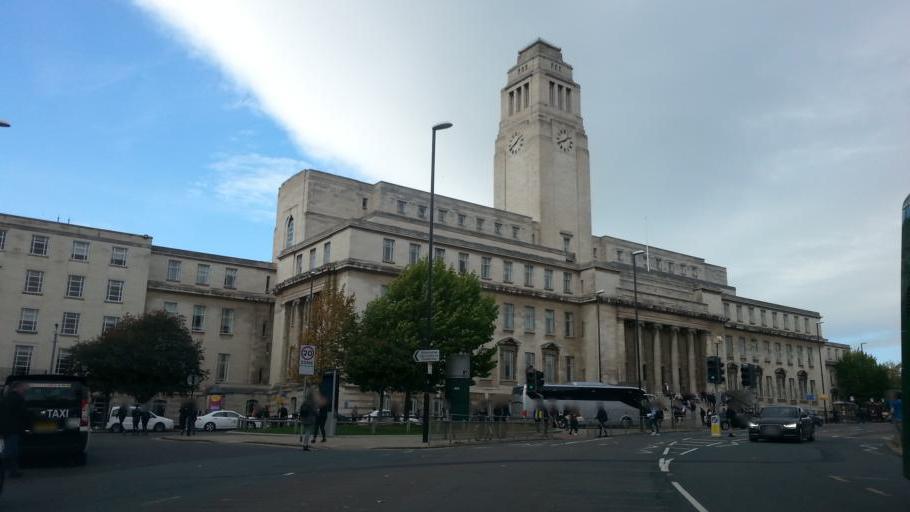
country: GB
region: England
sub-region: City and Borough of Leeds
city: Leeds
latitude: 53.8072
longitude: -1.5516
